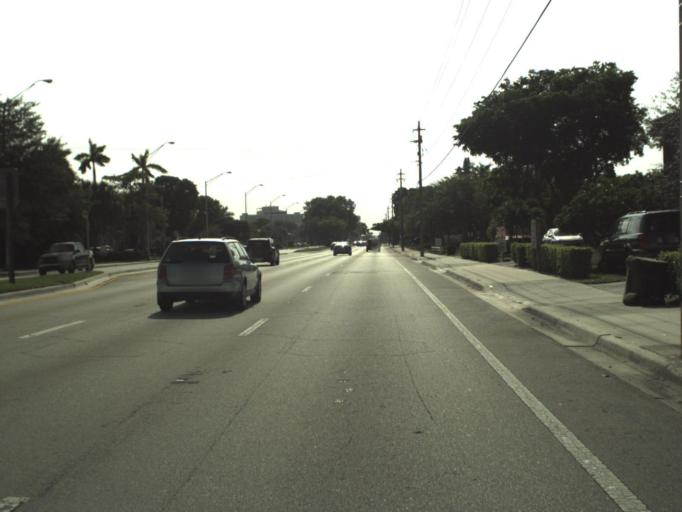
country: US
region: Florida
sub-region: Broward County
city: Coral Springs
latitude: 26.2724
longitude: -80.2411
